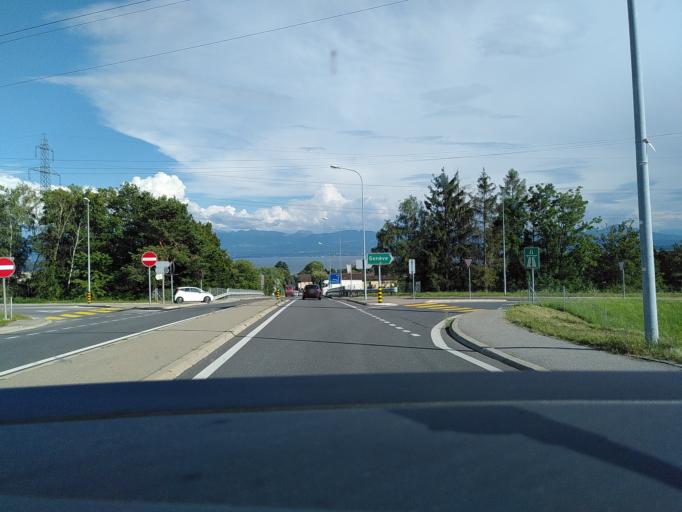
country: CH
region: Vaud
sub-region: Nyon District
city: Rolle
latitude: 46.4657
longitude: 6.3324
